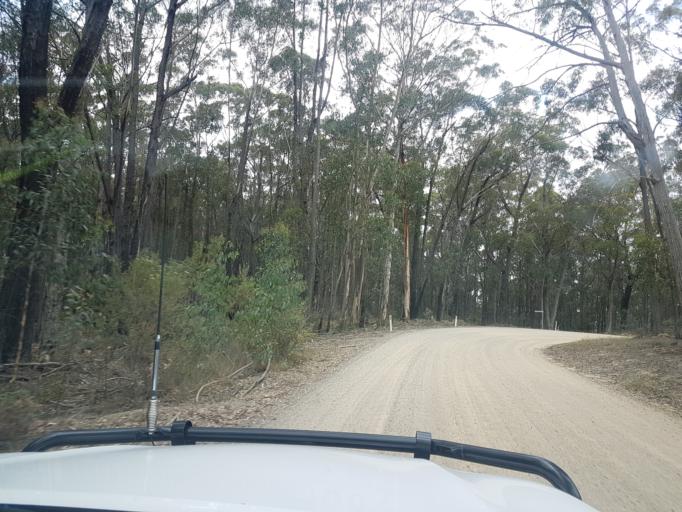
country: AU
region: Victoria
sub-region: East Gippsland
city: Bairnsdale
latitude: -37.6896
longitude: 147.5636
